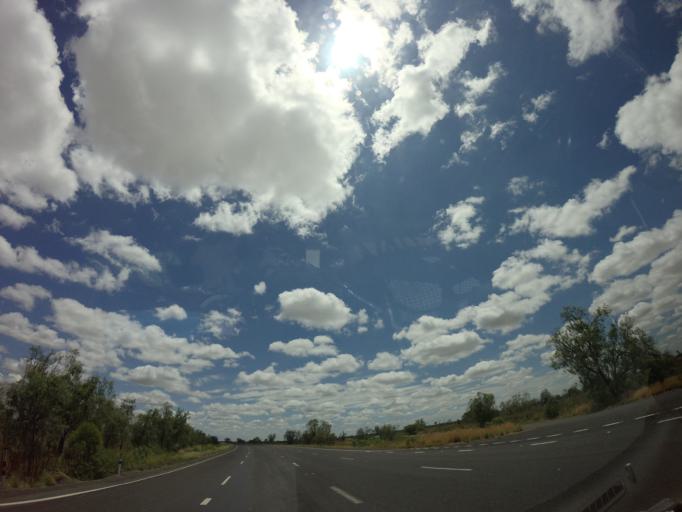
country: AU
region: New South Wales
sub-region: Moree Plains
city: Moree
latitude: -29.0371
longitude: 150.0553
